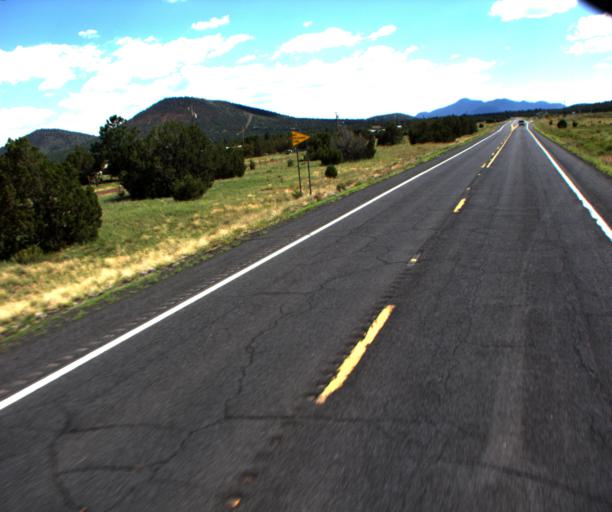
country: US
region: Arizona
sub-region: Coconino County
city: Williams
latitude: 35.3716
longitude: -112.1635
